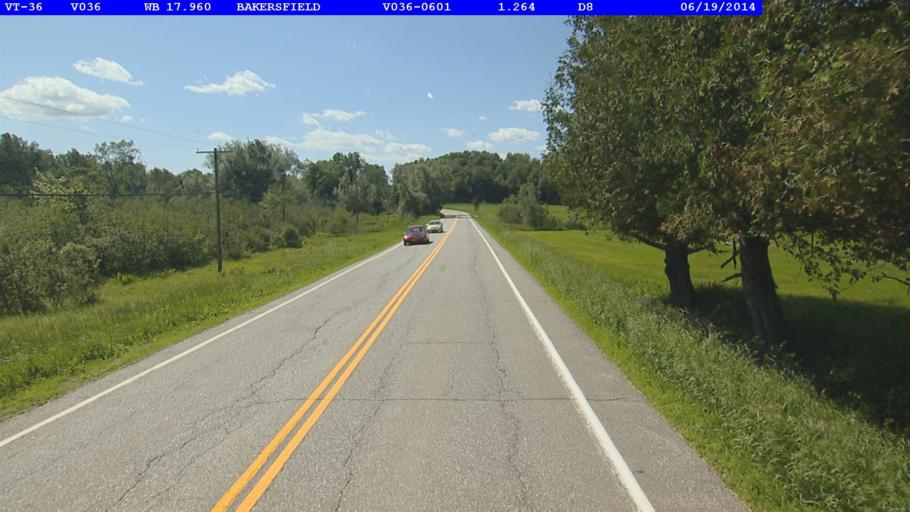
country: US
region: Vermont
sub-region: Franklin County
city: Enosburg Falls
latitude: 44.7824
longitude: -72.8256
